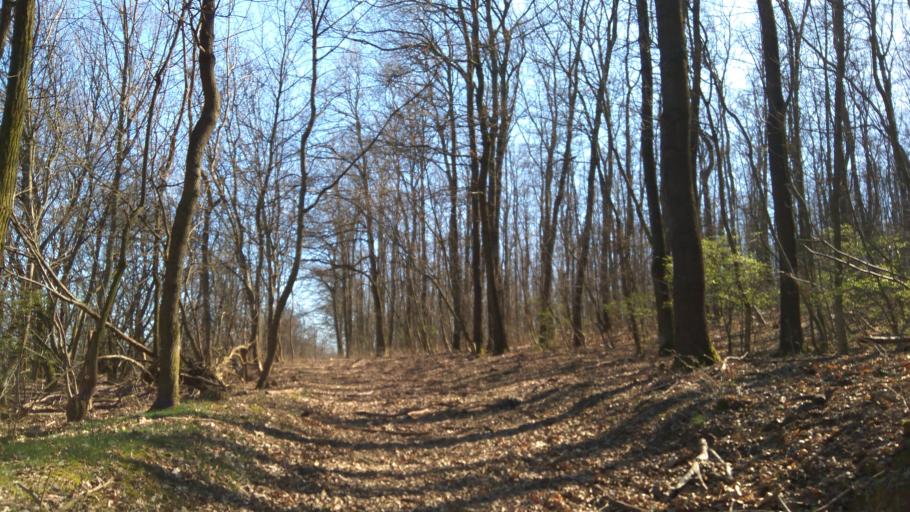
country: HU
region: Pest
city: Pilisborosjeno
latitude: 47.6314
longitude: 18.9918
